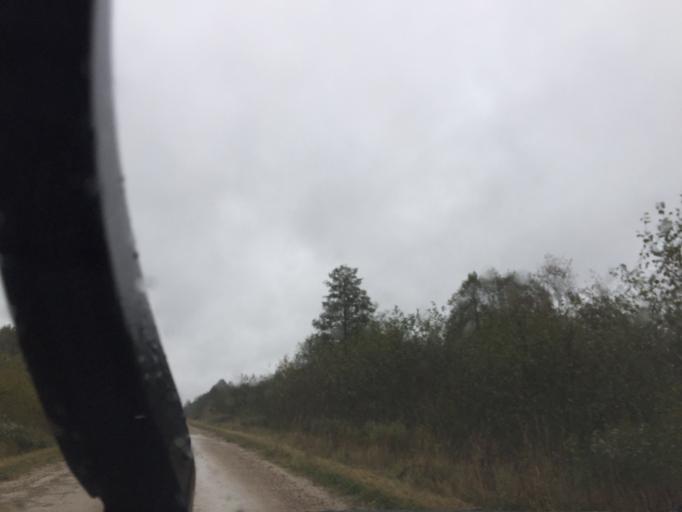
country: LV
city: Tireli
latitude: 56.7527
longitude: 23.5366
